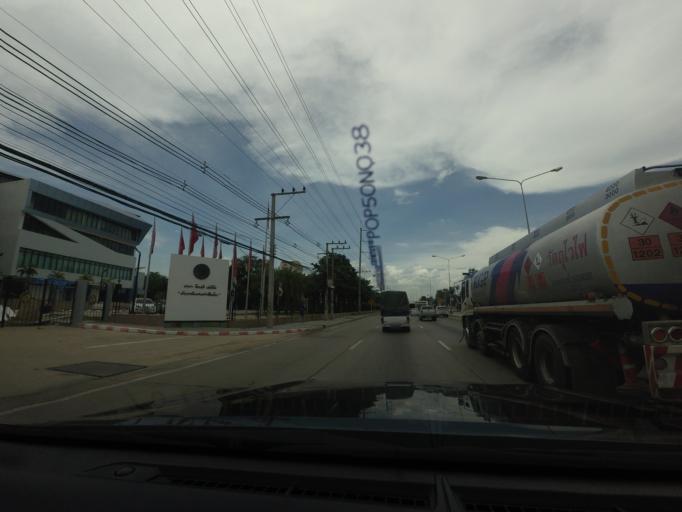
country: TH
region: Nakhon Pathom
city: Nakhon Pathom
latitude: 13.8360
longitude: 100.0320
